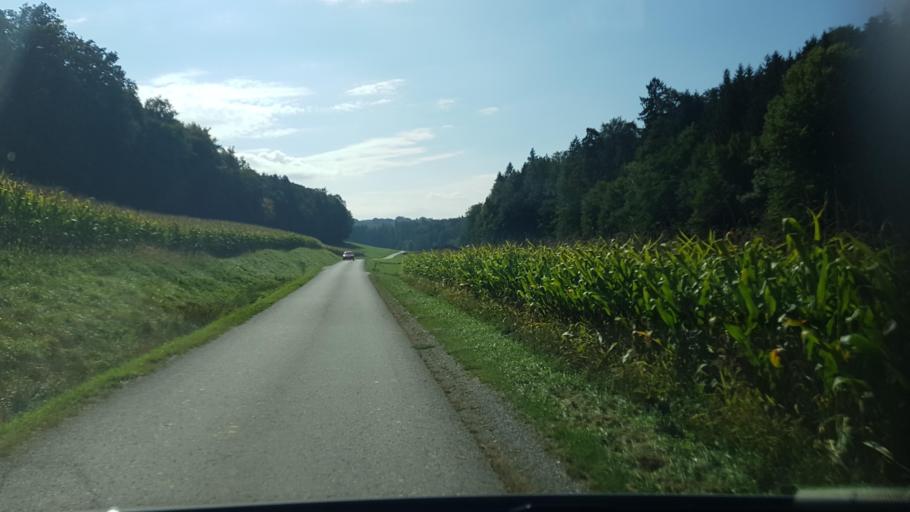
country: AT
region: Styria
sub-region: Politischer Bezirk Deutschlandsberg
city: Wettmannstatten
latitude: 46.8177
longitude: 15.3771
